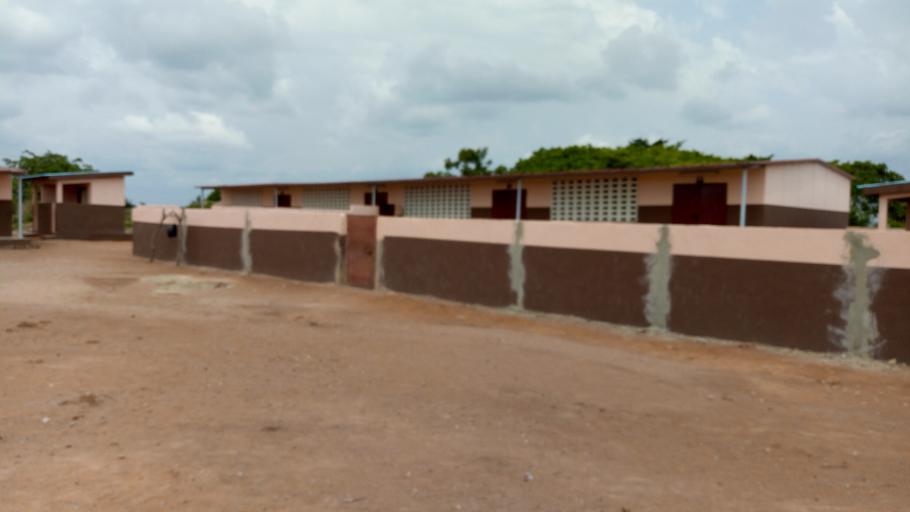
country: CI
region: Vallee du Bandama
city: Bouake
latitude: 7.7391
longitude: -5.0579
